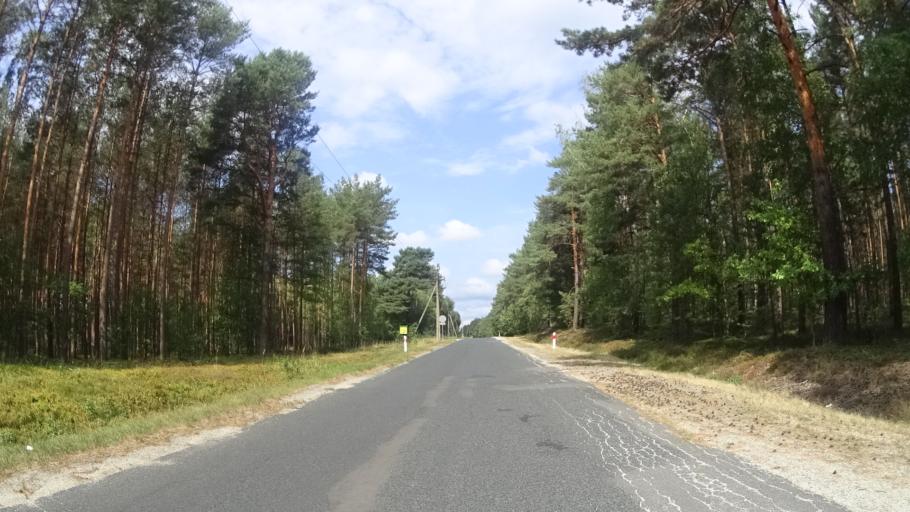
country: PL
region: Lubusz
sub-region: Powiat zarski
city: Leknica
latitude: 51.5293
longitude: 14.8178
